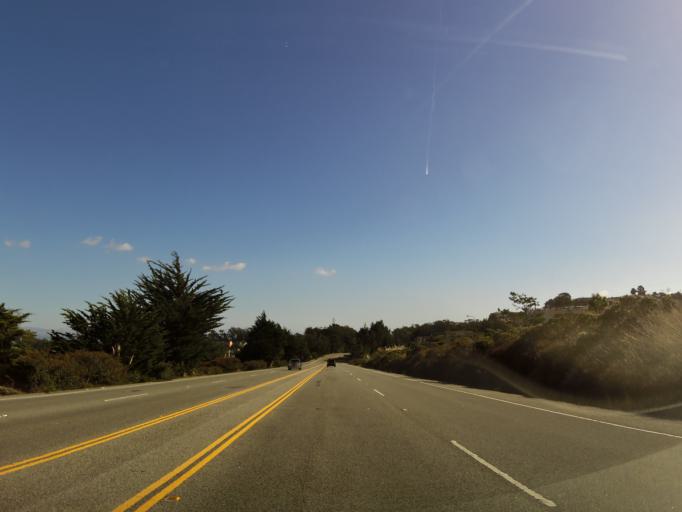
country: US
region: California
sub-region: San Mateo County
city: Pacifica
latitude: 37.6354
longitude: -122.4595
